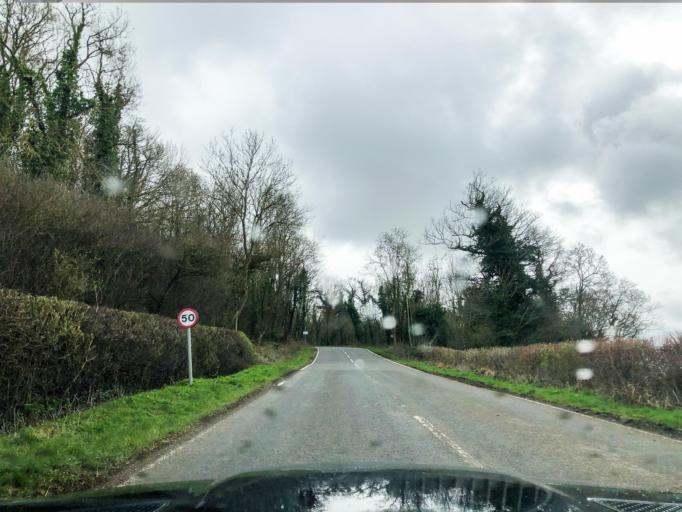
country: GB
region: England
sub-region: Oxfordshire
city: Hanwell
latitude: 52.1353
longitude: -1.4458
